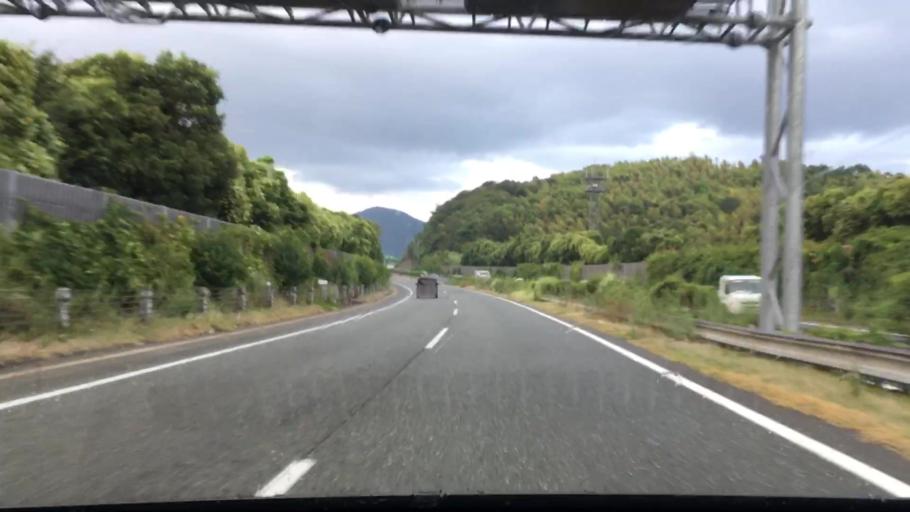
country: JP
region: Fukuoka
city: Kitakyushu
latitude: 33.8067
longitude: 130.8770
